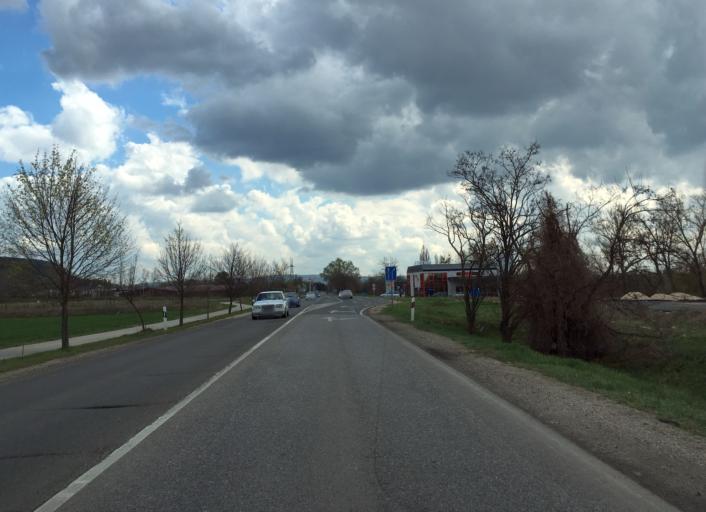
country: HU
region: Komarom-Esztergom
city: Vertesszolos
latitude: 47.6091
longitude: 18.3843
